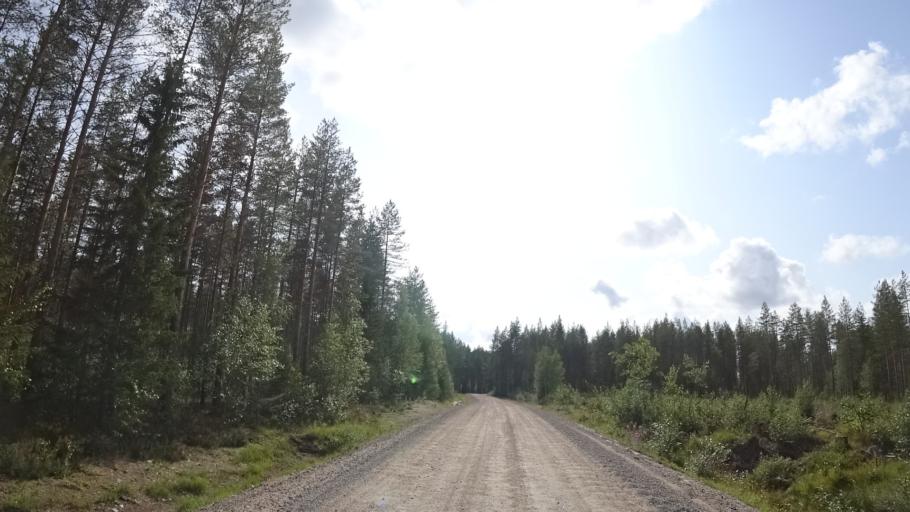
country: FI
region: North Karelia
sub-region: Pielisen Karjala
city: Lieksa
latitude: 63.5729
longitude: 30.1155
